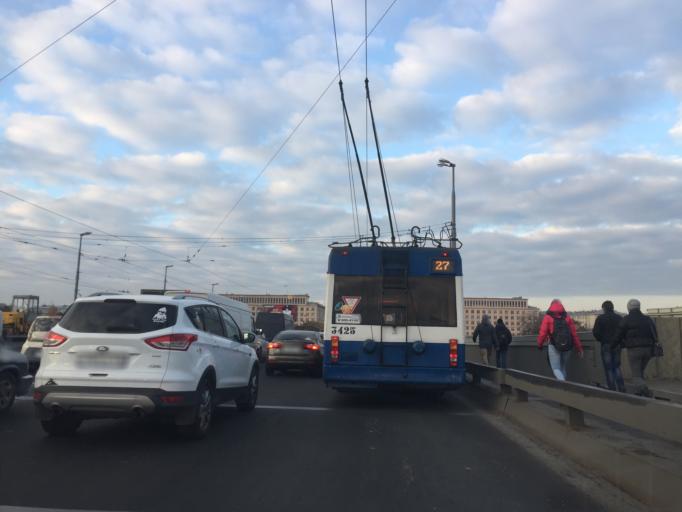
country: RU
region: St.-Petersburg
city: Obukhovo
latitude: 59.8778
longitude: 30.4525
